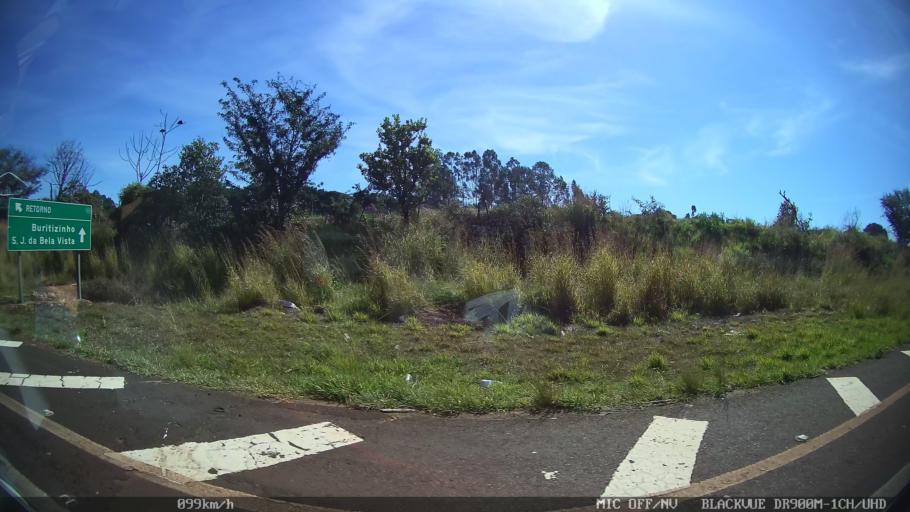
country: BR
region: Sao Paulo
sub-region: Franca
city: Franca
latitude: -20.5546
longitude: -47.4942
